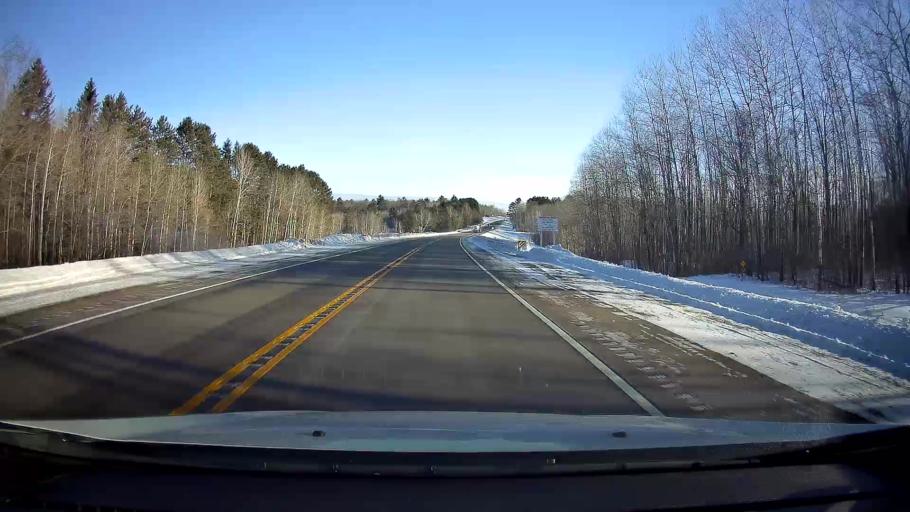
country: US
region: Wisconsin
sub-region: Sawyer County
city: Hayward
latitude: 46.0679
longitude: -91.4341
